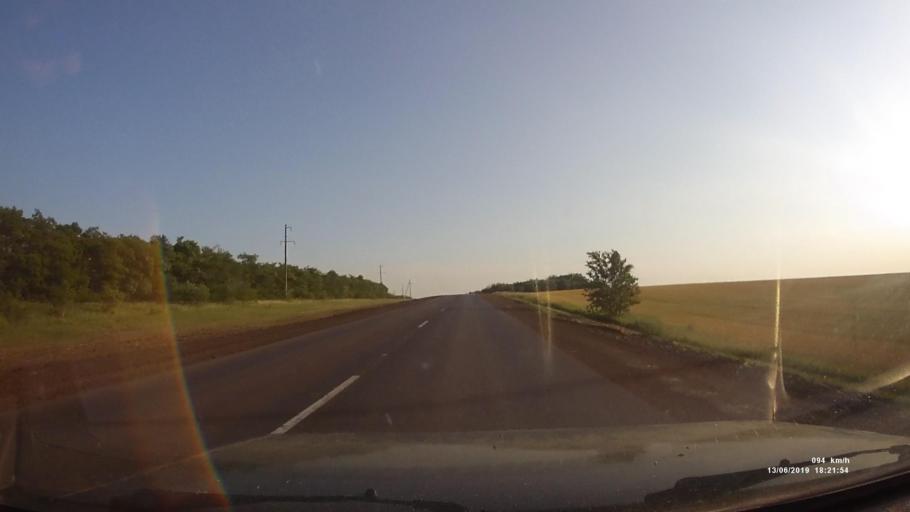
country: RU
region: Rostov
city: Kazanskaya
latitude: 49.8653
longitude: 41.2846
